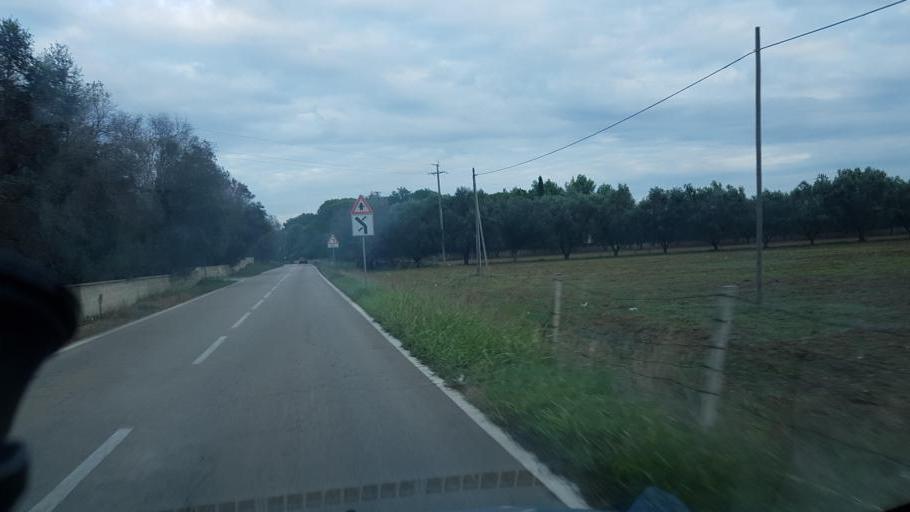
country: IT
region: Apulia
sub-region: Provincia di Brindisi
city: Oria
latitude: 40.5097
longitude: 17.6602
